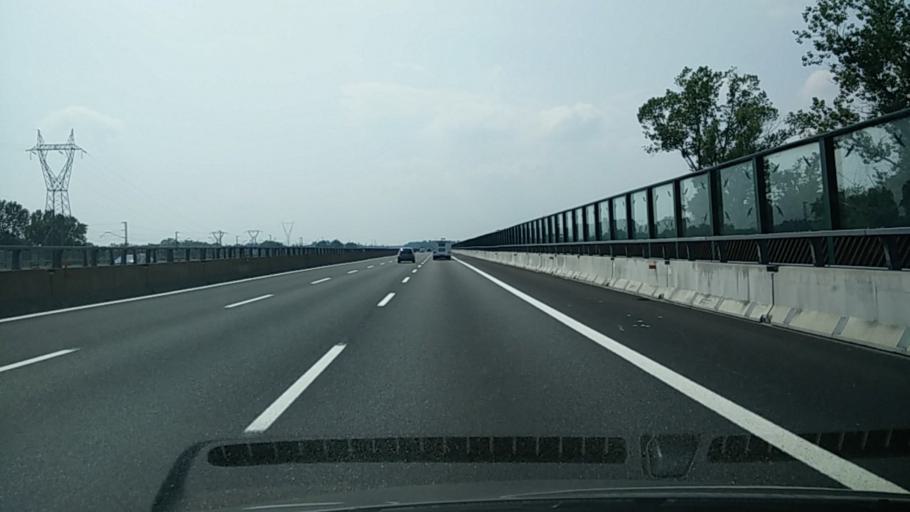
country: IT
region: Lombardy
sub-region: Citta metropolitana di Milano
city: Bernate Ticino
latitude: 45.4699
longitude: 8.7958
